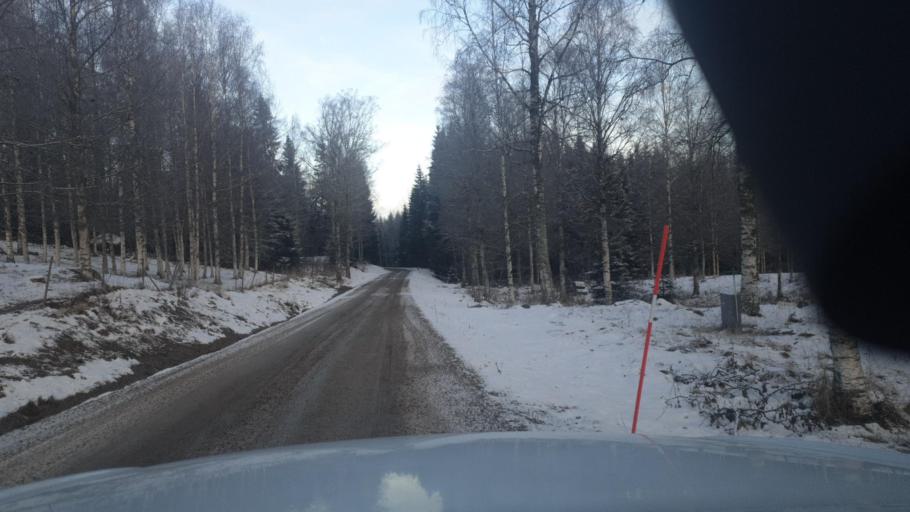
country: SE
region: Vaermland
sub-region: Arvika Kommun
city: Arvika
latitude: 59.9995
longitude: 12.6590
